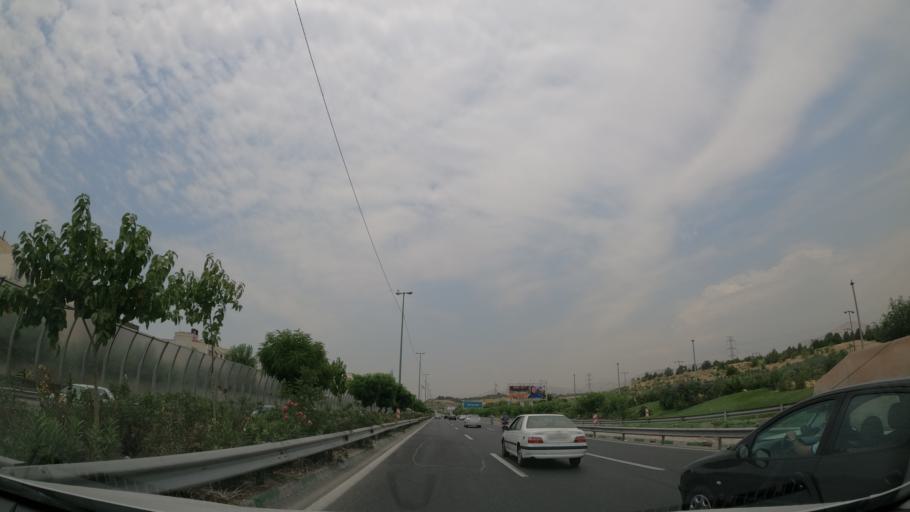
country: IR
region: Tehran
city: Tehran
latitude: 35.7397
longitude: 51.3553
